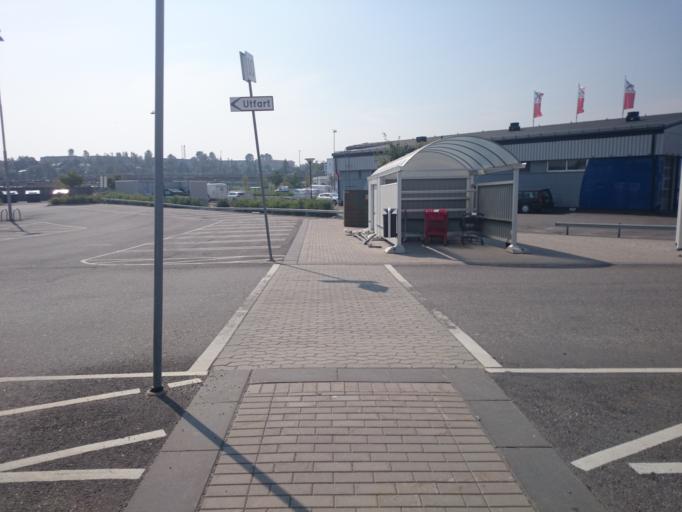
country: SE
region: Vaesternorrland
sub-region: Haernoesands Kommun
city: Haernoesand
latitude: 62.6361
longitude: 17.9276
